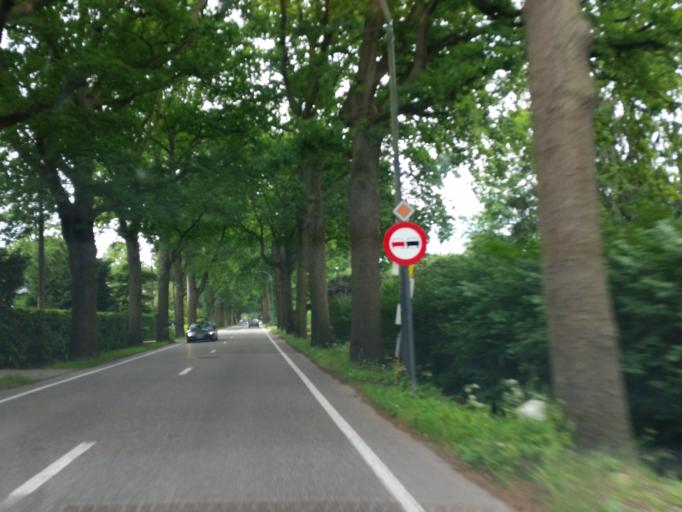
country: BE
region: Flanders
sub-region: Provincie Antwerpen
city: Schilde
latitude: 51.2440
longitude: 4.5745
